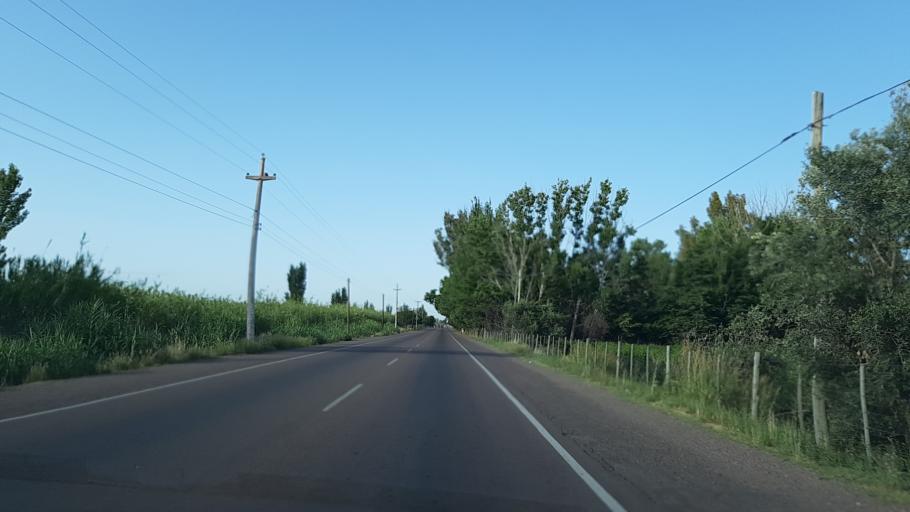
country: AR
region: Mendoza
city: San Martin
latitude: -32.9803
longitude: -68.4592
